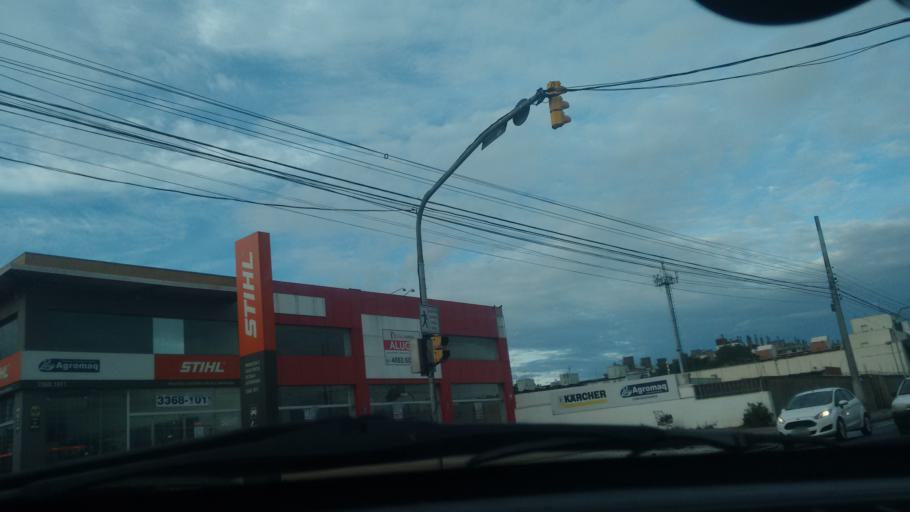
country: BR
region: Rio Grande do Sul
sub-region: Cachoeirinha
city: Cachoeirinha
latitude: -29.9979
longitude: -51.1463
